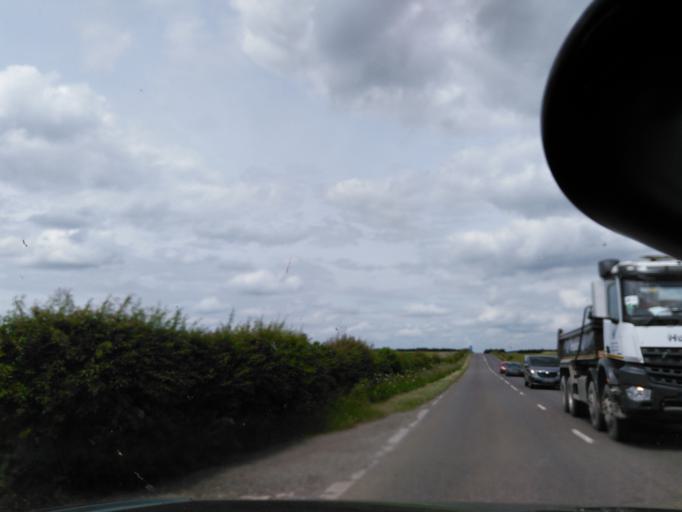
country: GB
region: England
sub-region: Wiltshire
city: Winterbourne Stoke
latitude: 51.1775
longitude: -1.8596
